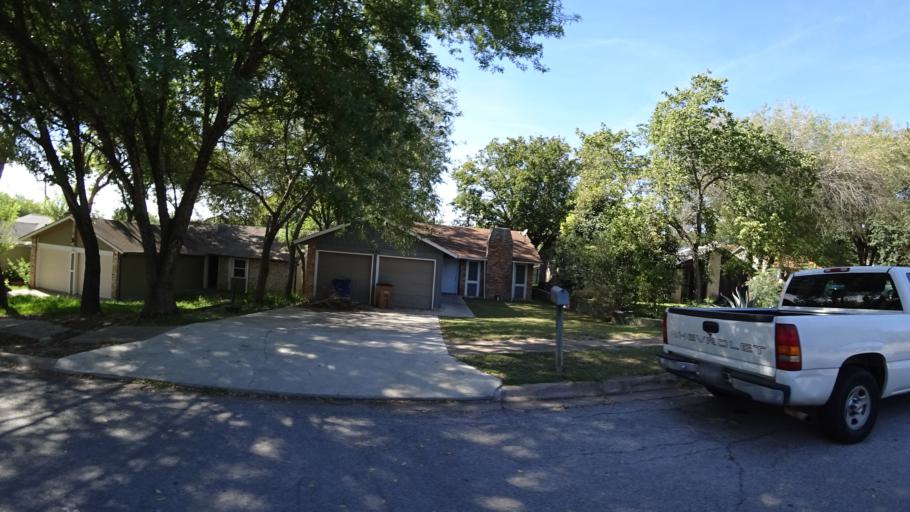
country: US
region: Texas
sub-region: Travis County
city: Austin
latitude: 30.1973
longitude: -97.7472
